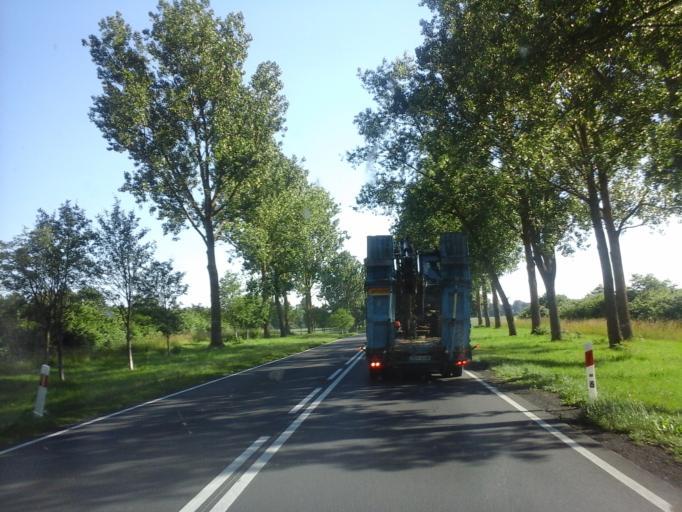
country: PL
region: West Pomeranian Voivodeship
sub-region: Powiat gryficki
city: Ploty
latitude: 53.7837
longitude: 15.2495
